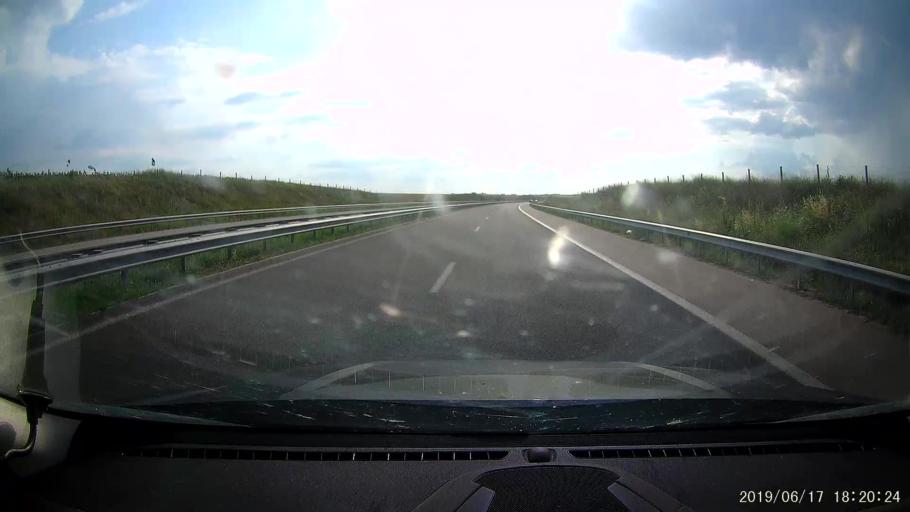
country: BG
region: Khaskovo
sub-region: Obshtina Simeonovgrad
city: Simeonovgrad
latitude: 41.9617
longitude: 25.8152
